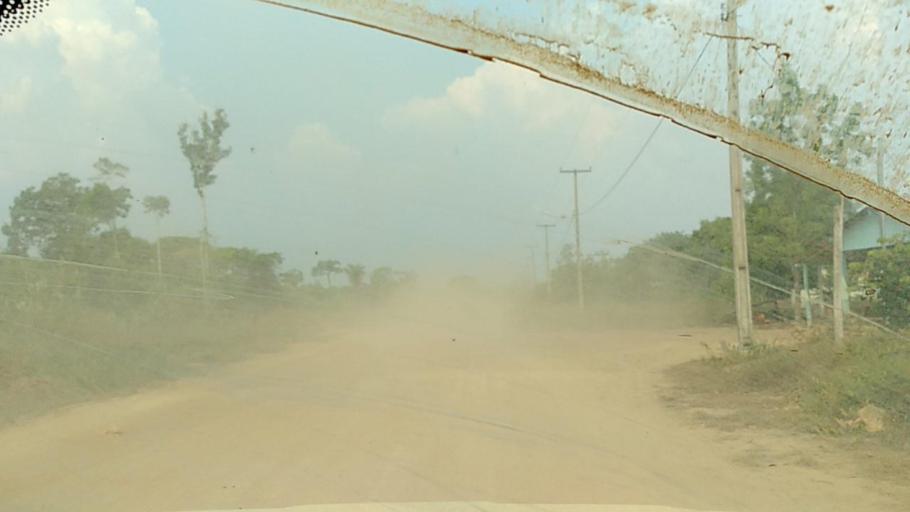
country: BR
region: Rondonia
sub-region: Porto Velho
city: Porto Velho
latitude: -8.6835
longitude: -63.1874
